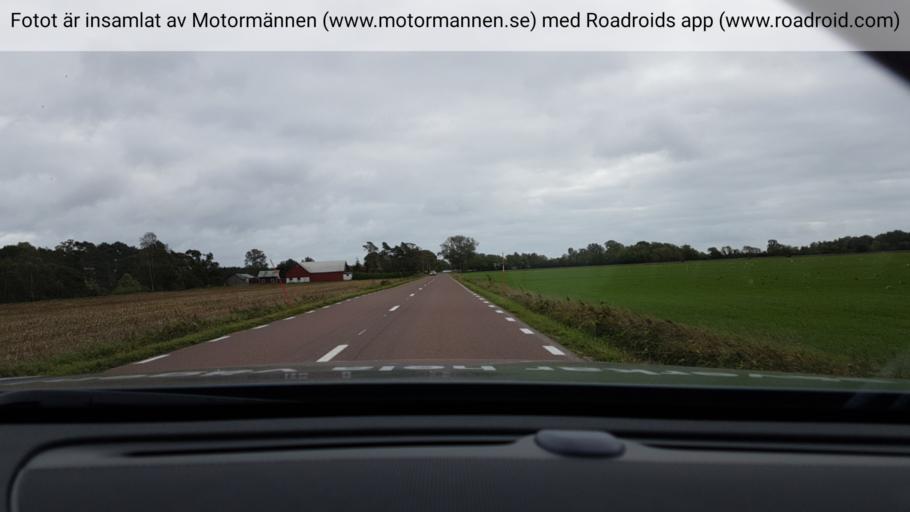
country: SE
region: Gotland
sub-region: Gotland
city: Hemse
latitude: 57.1652
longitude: 18.2706
